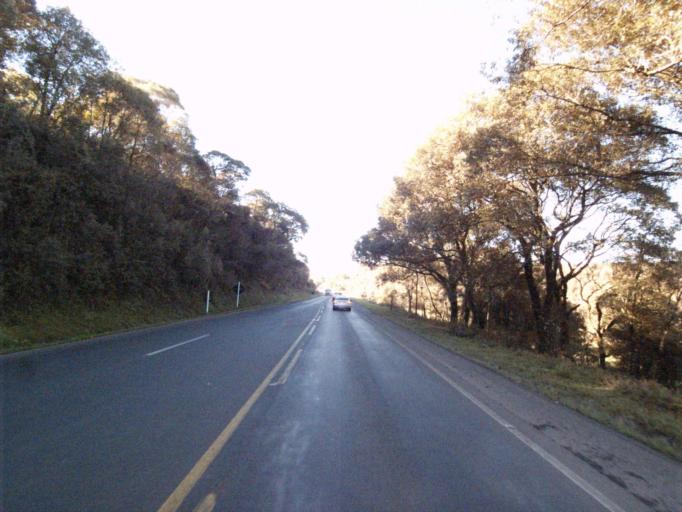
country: BR
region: Santa Catarina
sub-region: Concordia
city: Concordia
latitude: -26.8985
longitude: -51.9764
